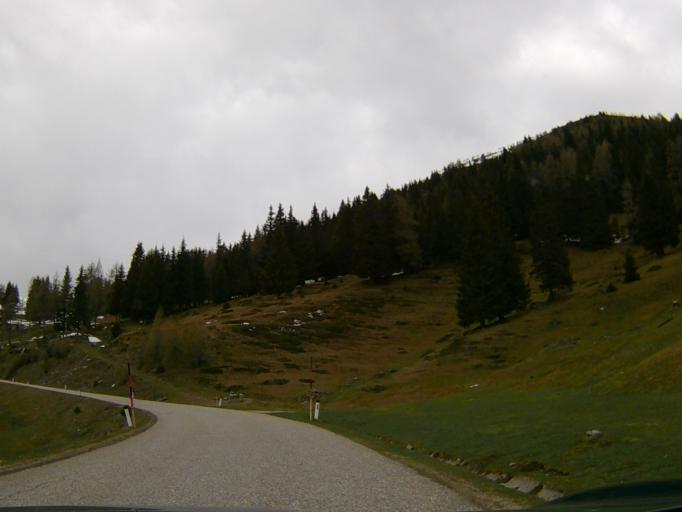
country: AT
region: Carinthia
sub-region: Politischer Bezirk Villach Land
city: Stockenboi
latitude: 46.7512
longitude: 13.4826
